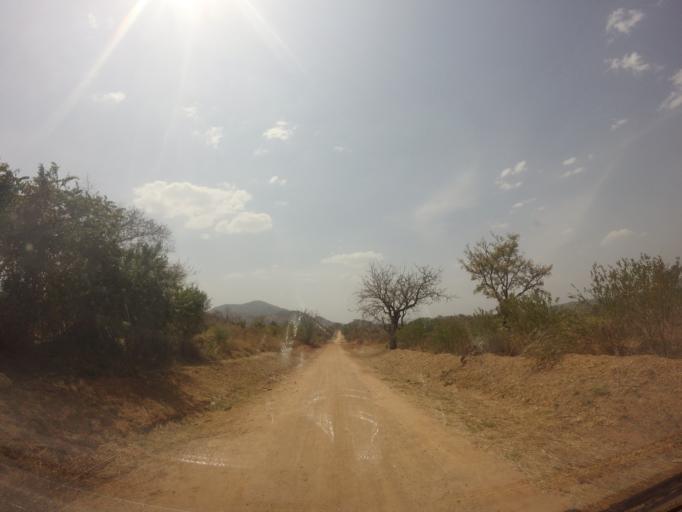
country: UG
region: Northern Region
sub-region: Arua District
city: Arua
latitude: 2.8968
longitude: 31.1193
